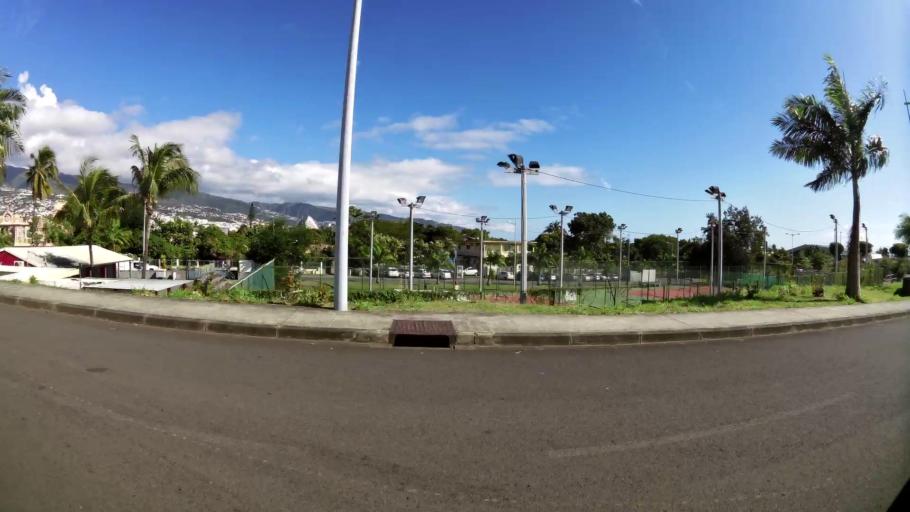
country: RE
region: Reunion
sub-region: Reunion
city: Sainte-Marie
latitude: -20.8976
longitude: 55.5020
